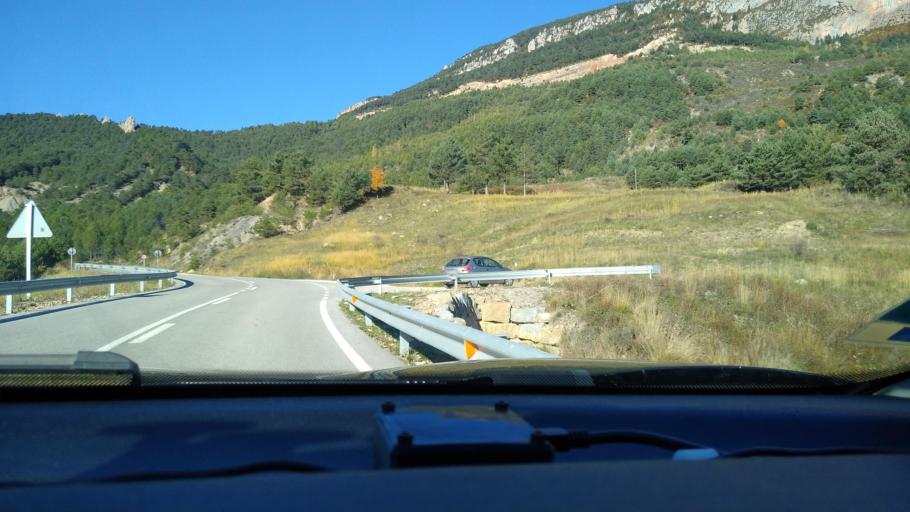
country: ES
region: Catalonia
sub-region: Provincia de Barcelona
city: Saldes
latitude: 42.2213
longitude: 1.7205
